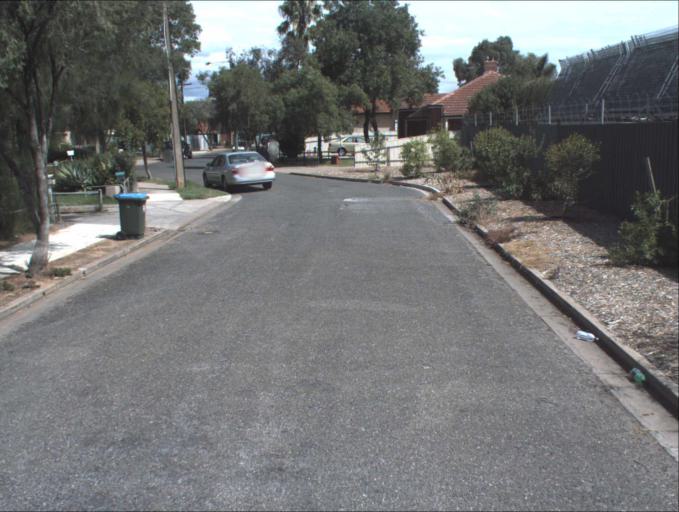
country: AU
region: South Australia
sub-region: Port Adelaide Enfield
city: Blair Athol
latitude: -34.8570
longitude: 138.5792
